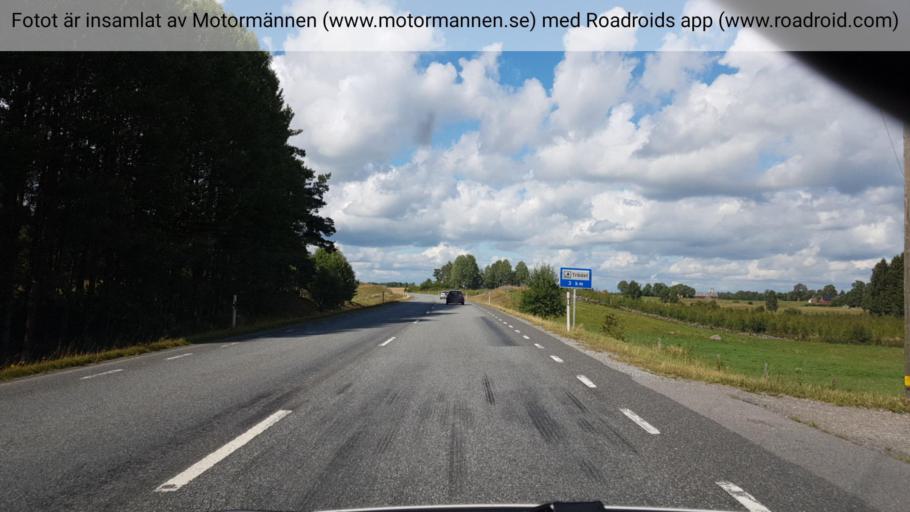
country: SE
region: Vaestra Goetaland
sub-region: Falkopings Kommun
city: Falkoeping
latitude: 57.9711
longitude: 13.5299
